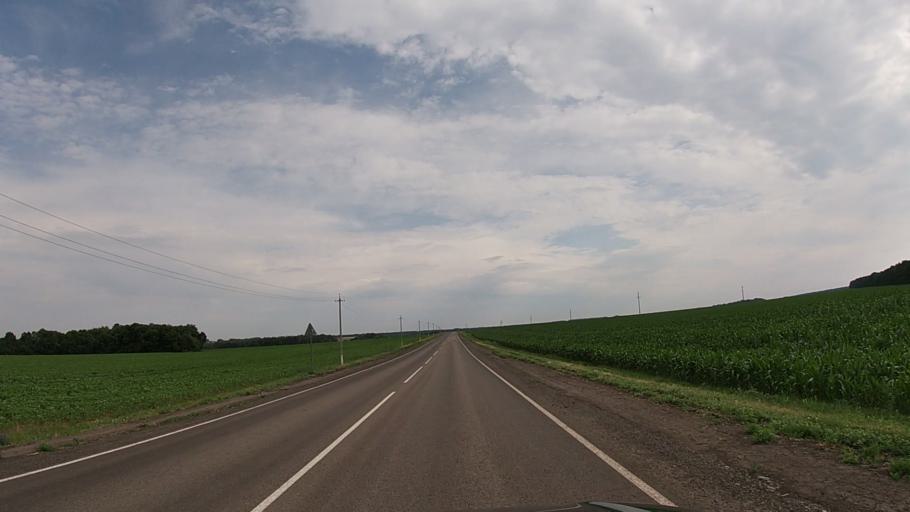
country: RU
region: Belgorod
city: Krasnaya Yaruga
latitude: 50.8150
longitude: 35.5017
